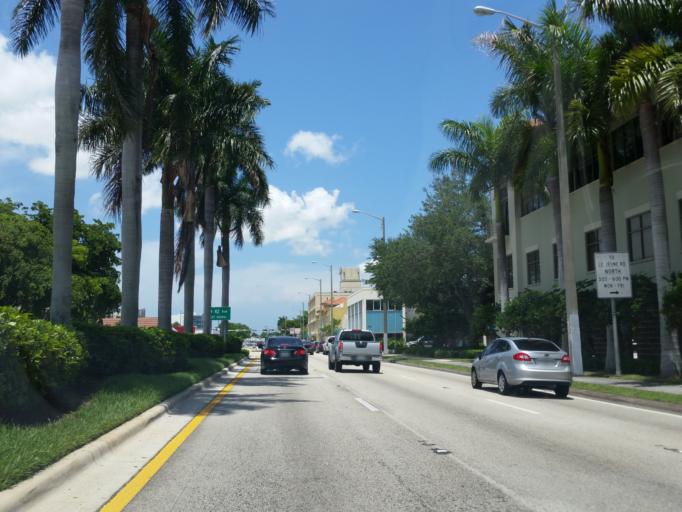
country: US
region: Florida
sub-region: Miami-Dade County
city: Coral Gables
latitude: 25.7246
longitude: -80.2640
